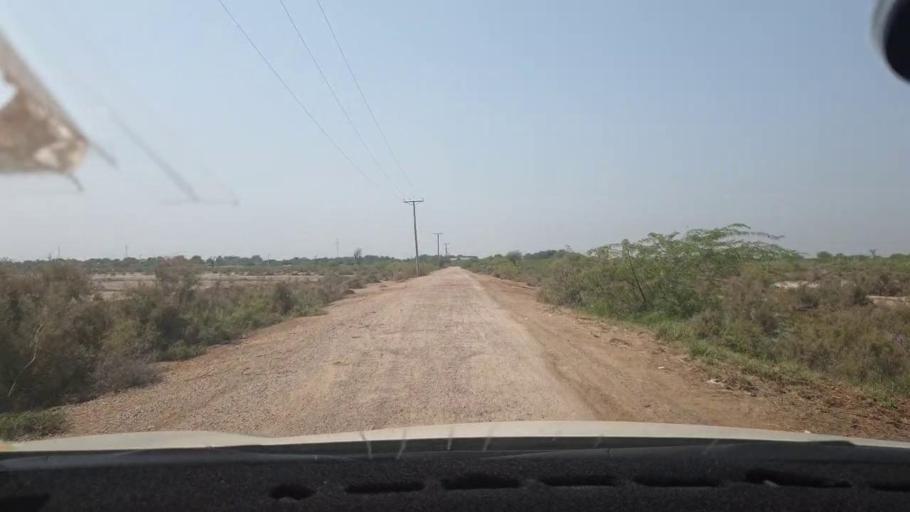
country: PK
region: Sindh
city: Tando Mittha Khan
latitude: 25.9213
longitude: 69.2493
